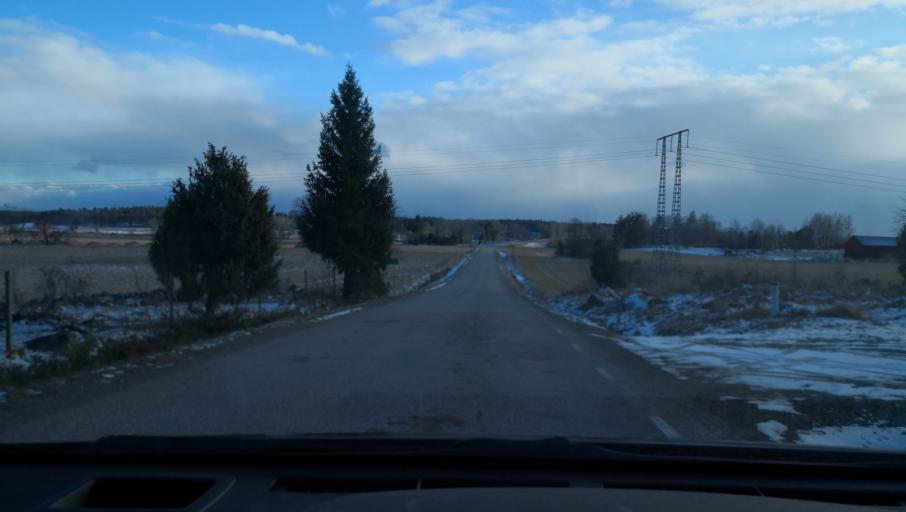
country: SE
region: Uppsala
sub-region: Enkopings Kommun
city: Irsta
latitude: 59.6705
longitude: 16.8381
